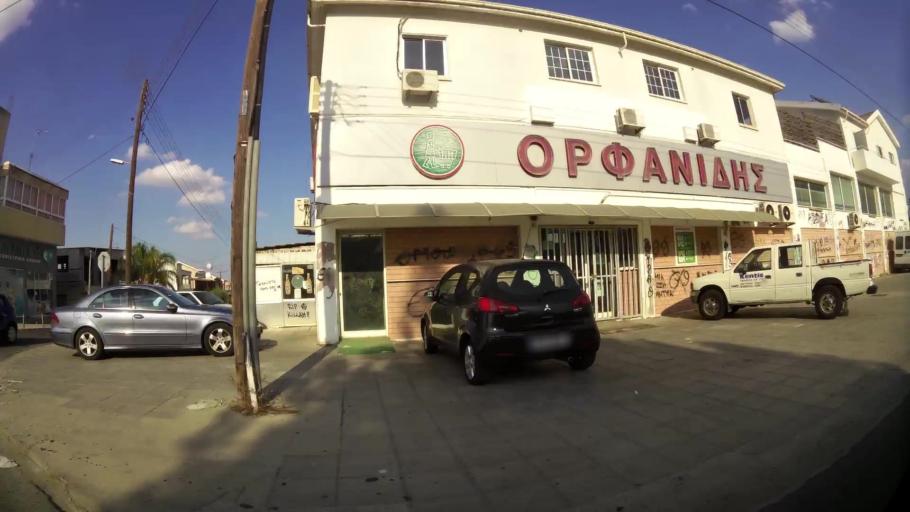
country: CY
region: Lefkosia
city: Kato Deftera
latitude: 35.1128
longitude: 33.2910
